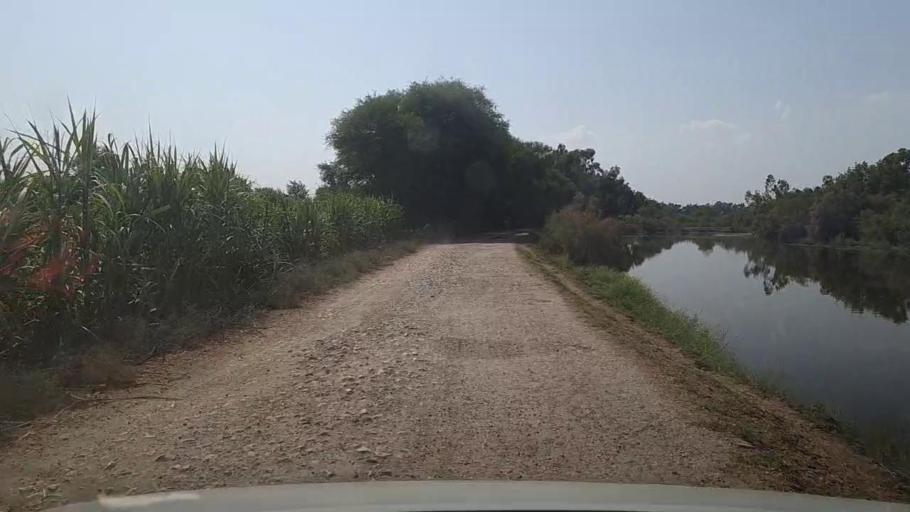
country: PK
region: Sindh
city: Khairpur
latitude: 28.1213
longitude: 69.6078
